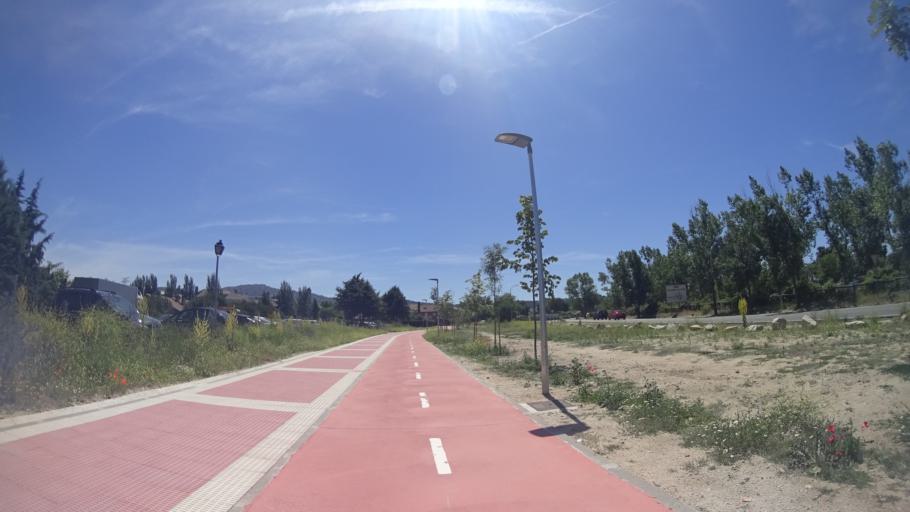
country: ES
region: Madrid
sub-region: Provincia de Madrid
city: Collado-Villalba
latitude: 40.6521
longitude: -4.0017
